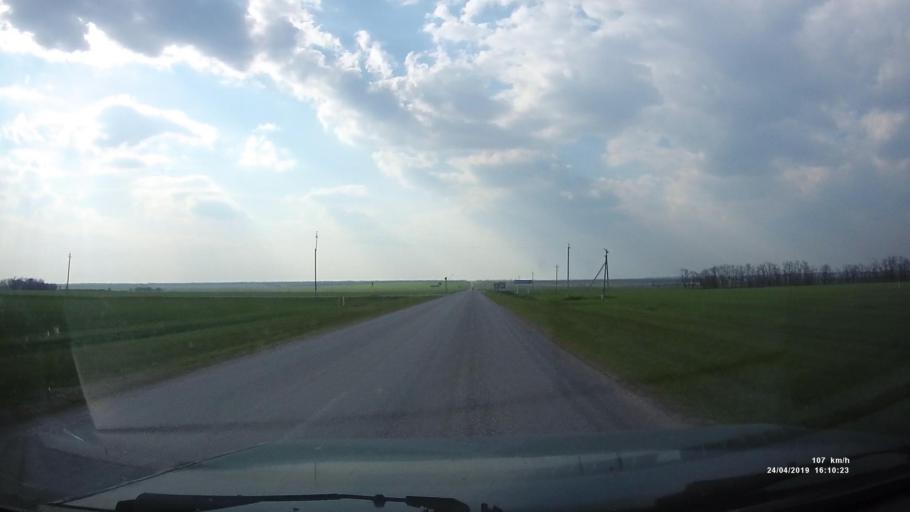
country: RU
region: Rostov
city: Sovetskoye
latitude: 46.7174
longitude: 42.2697
